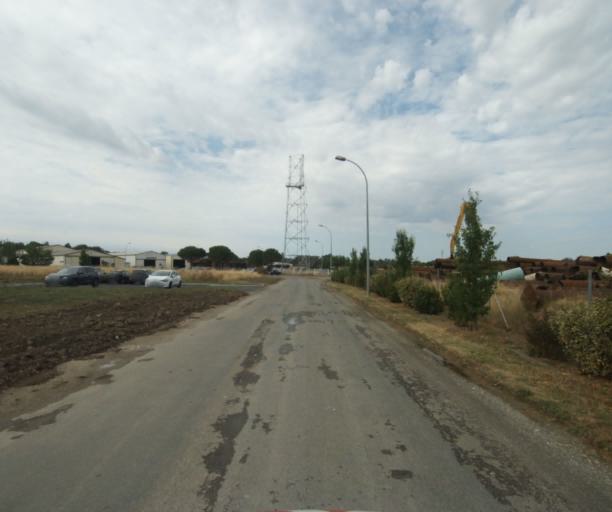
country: FR
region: Midi-Pyrenees
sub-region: Departement de la Haute-Garonne
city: Revel
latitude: 43.4559
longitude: 1.9763
